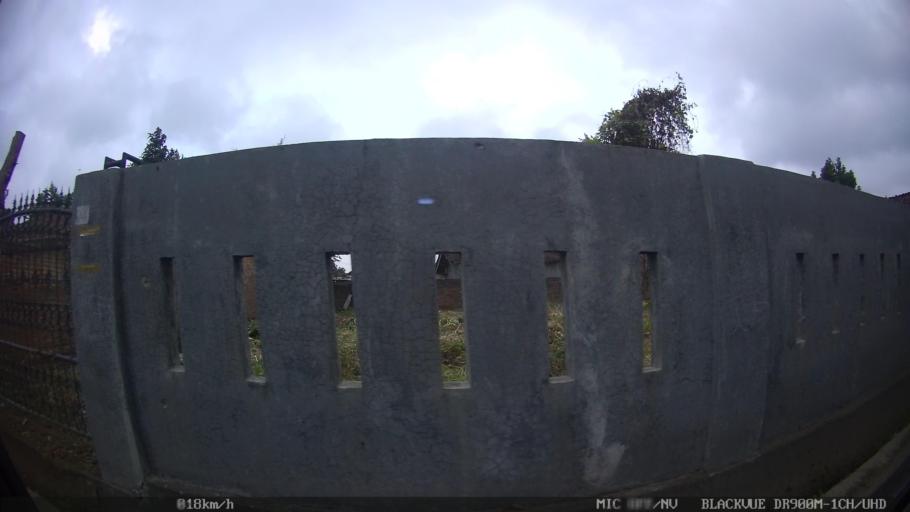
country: ID
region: Lampung
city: Bandarlampung
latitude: -5.4108
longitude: 105.2749
